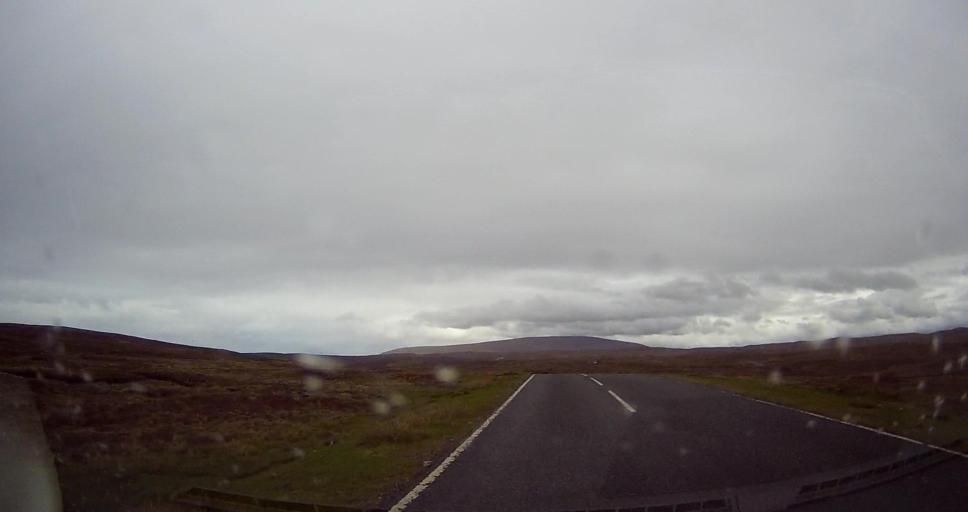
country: GB
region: Scotland
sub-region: Shetland Islands
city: Lerwick
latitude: 60.4900
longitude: -1.5860
